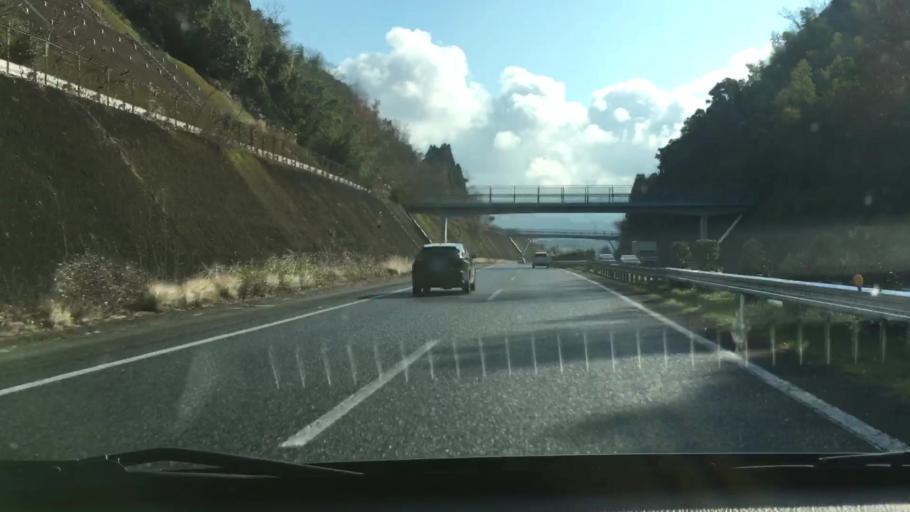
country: JP
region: Kumamoto
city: Matsubase
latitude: 32.5895
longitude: 130.7163
